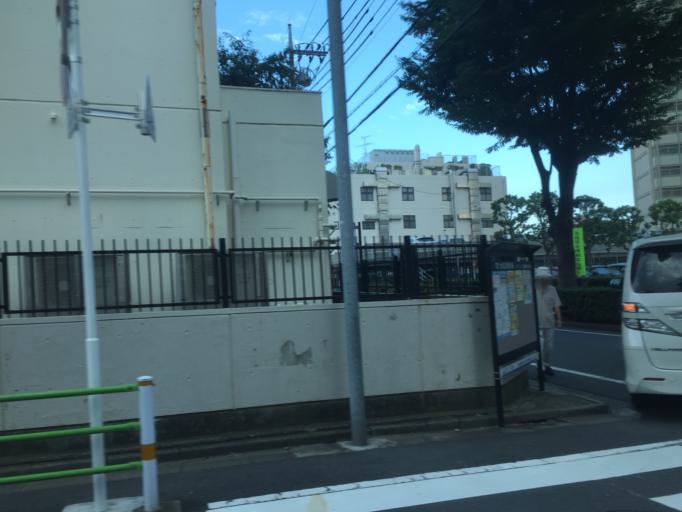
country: JP
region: Kanagawa
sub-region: Kawasaki-shi
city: Kawasaki
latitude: 35.5631
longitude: 139.6856
